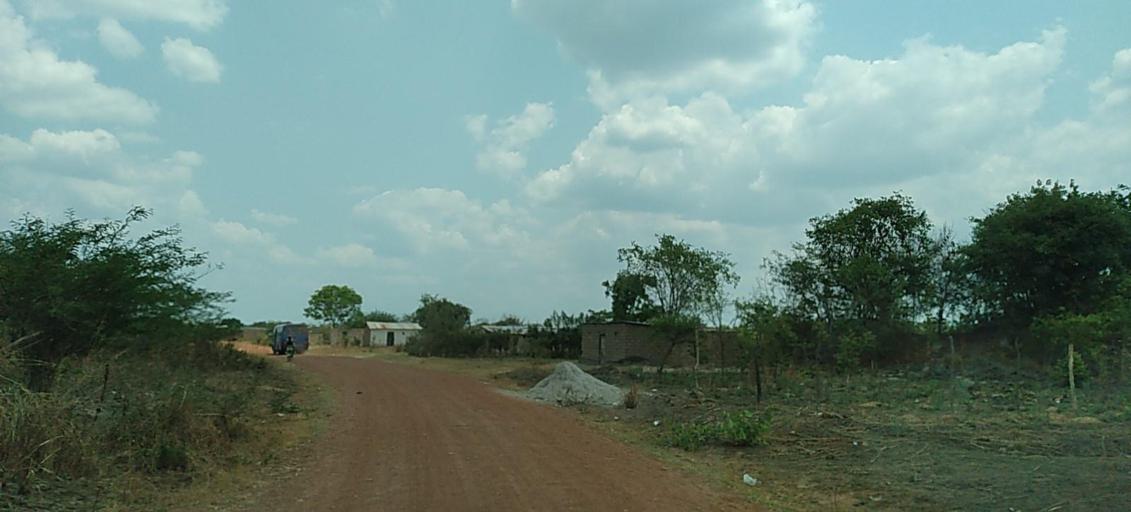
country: ZM
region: Copperbelt
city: Luanshya
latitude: -13.1263
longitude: 28.3105
